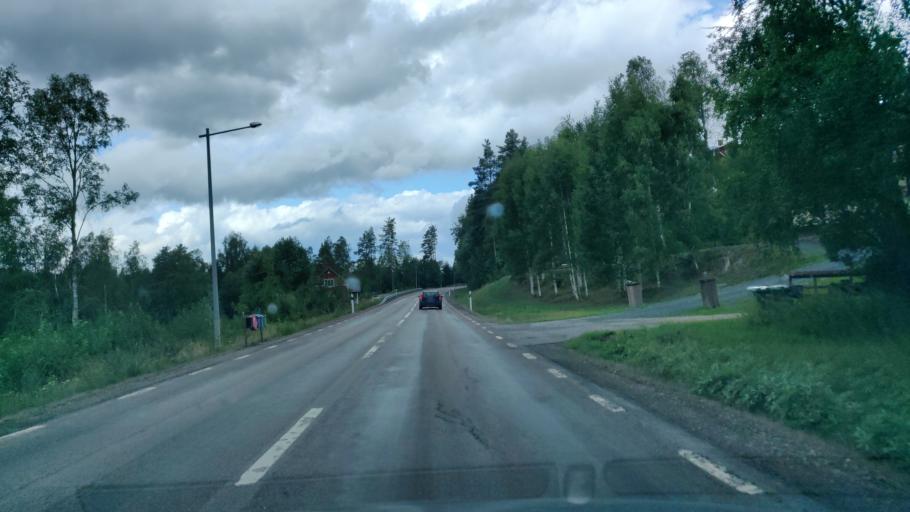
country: SE
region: Vaermland
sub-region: Torsby Kommun
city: Torsby
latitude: 60.5987
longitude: 13.0674
